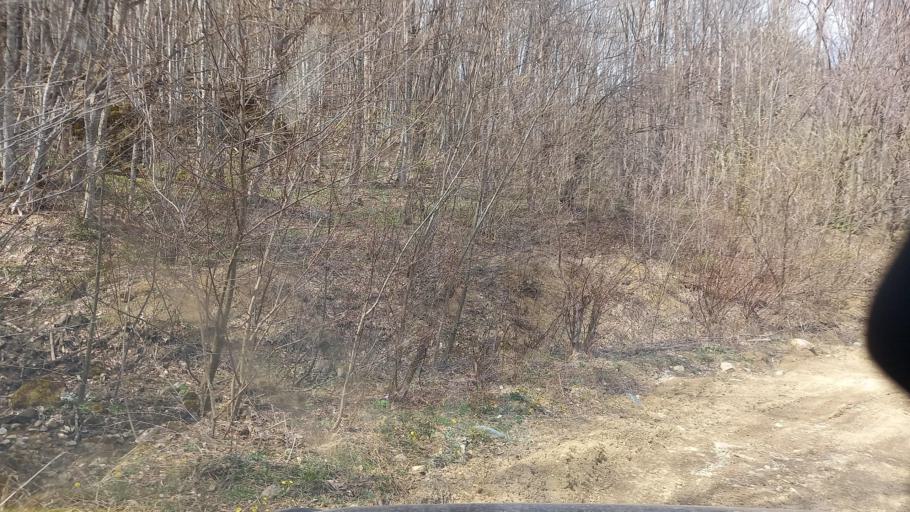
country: RU
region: Adygeya
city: Kamennomostskiy
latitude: 44.1099
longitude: 40.0918
